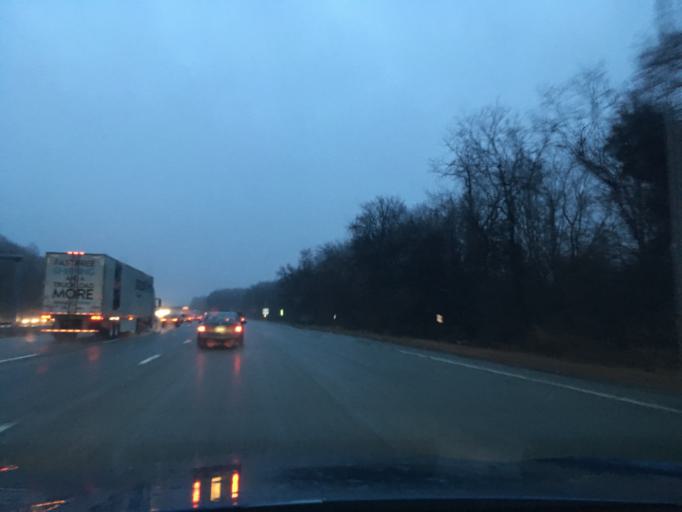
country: US
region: Rhode Island
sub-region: Kent County
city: East Greenwich
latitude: 41.6914
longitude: -71.4774
